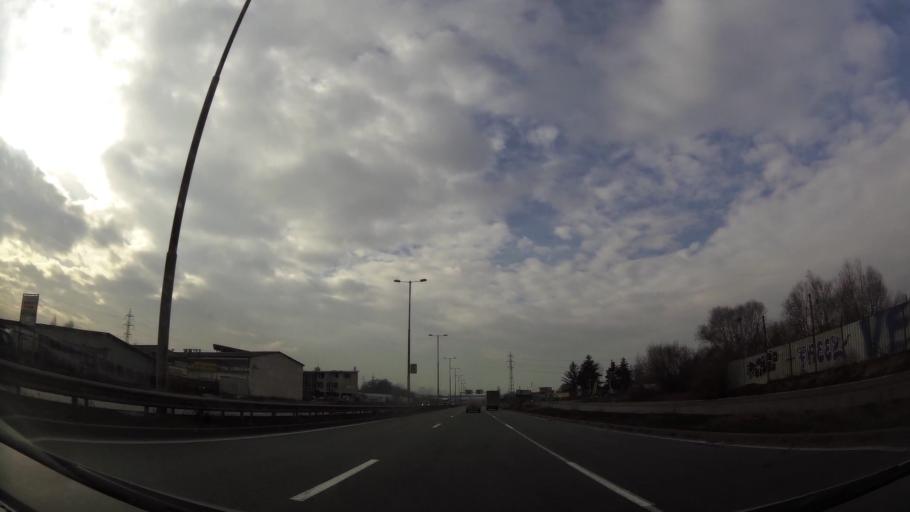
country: BG
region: Sofiya
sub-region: Obshtina Bozhurishte
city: Bozhurishte
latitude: 42.7402
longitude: 23.2517
